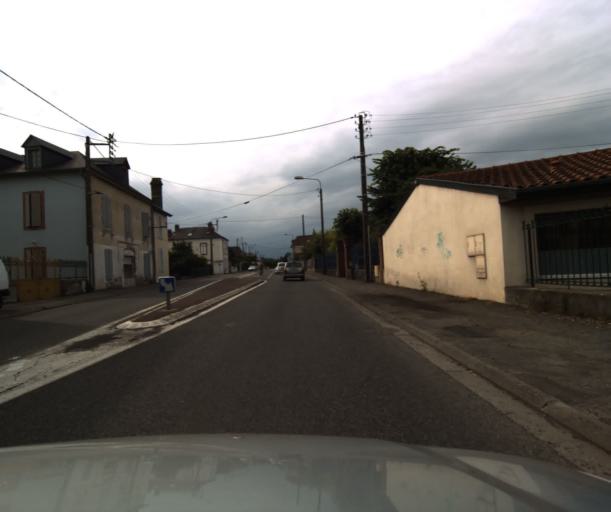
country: FR
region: Midi-Pyrenees
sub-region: Departement des Hautes-Pyrenees
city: Tarbes
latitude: 43.2317
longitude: 0.0935
